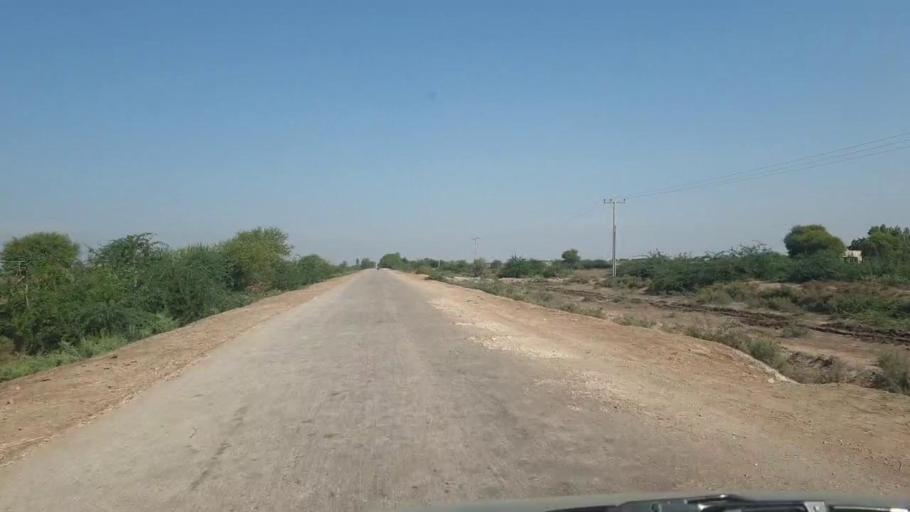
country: PK
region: Sindh
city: Tando Bago
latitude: 24.8081
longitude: 68.9803
